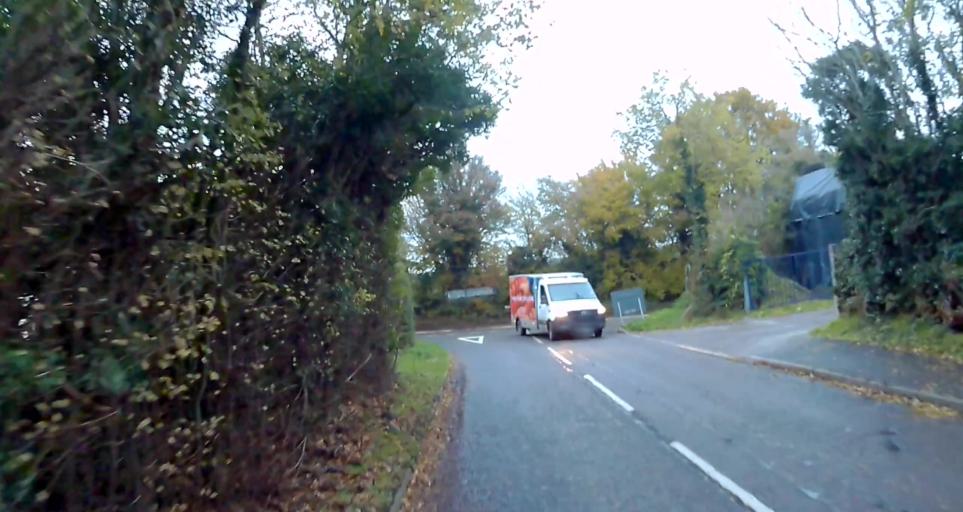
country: GB
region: England
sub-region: Hampshire
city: Odiham
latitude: 51.2542
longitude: -0.9578
